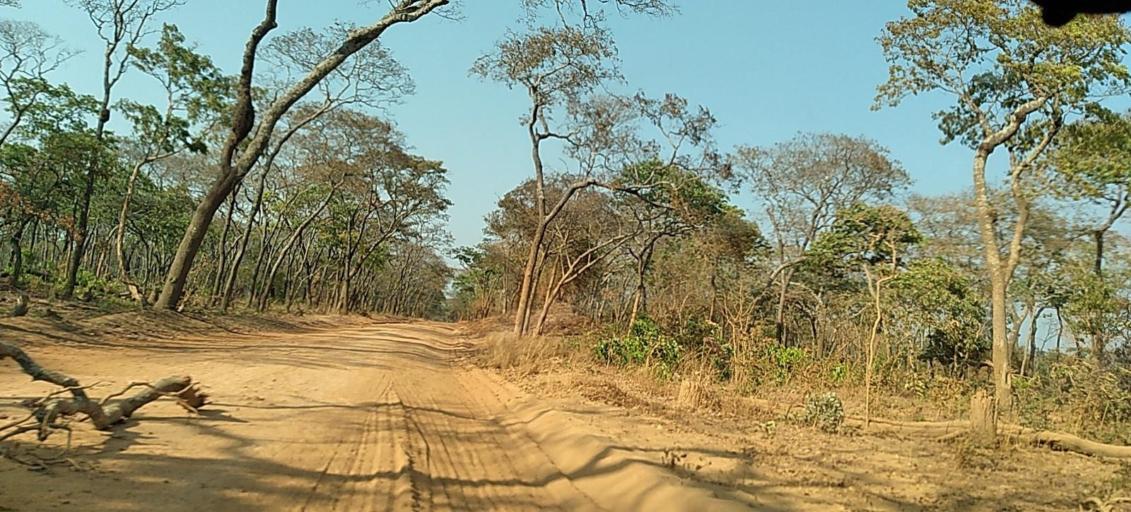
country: ZM
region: North-Western
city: Kasempa
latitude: -13.5923
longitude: 25.9831
